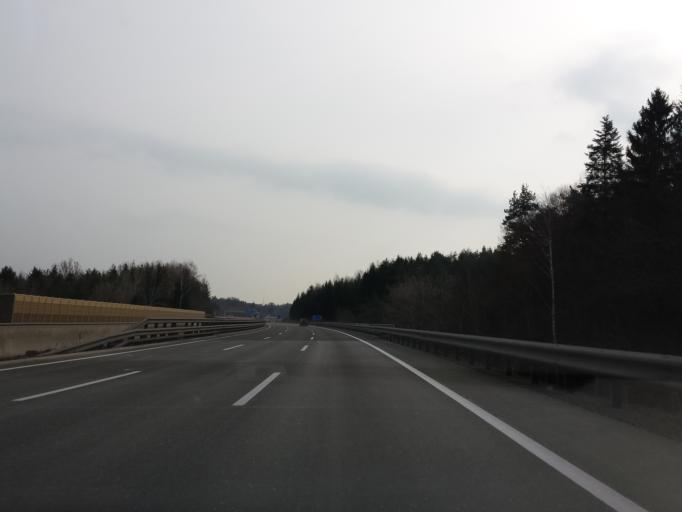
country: AT
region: Styria
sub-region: Politischer Bezirk Graz-Umgebung
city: Nestelbach bei Graz
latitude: 47.0625
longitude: 15.5699
